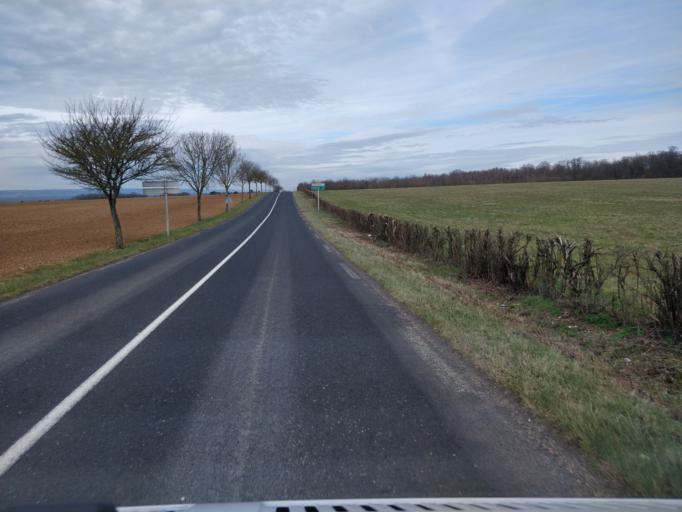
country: FR
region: Lorraine
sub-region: Departement de Meurthe-et-Moselle
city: Montauville
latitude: 48.9307
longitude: 5.8992
